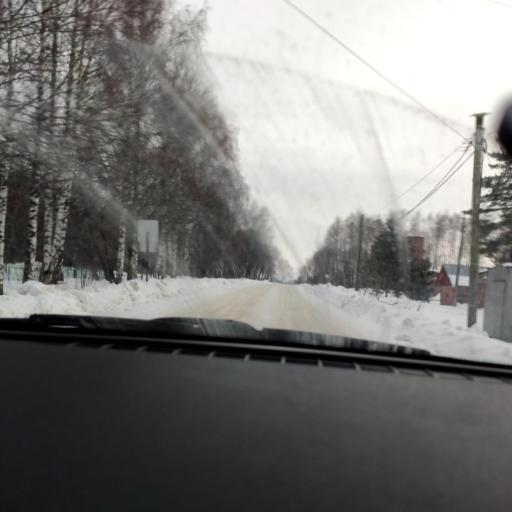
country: RU
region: Bashkortostan
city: Iglino
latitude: 54.7680
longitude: 56.5335
